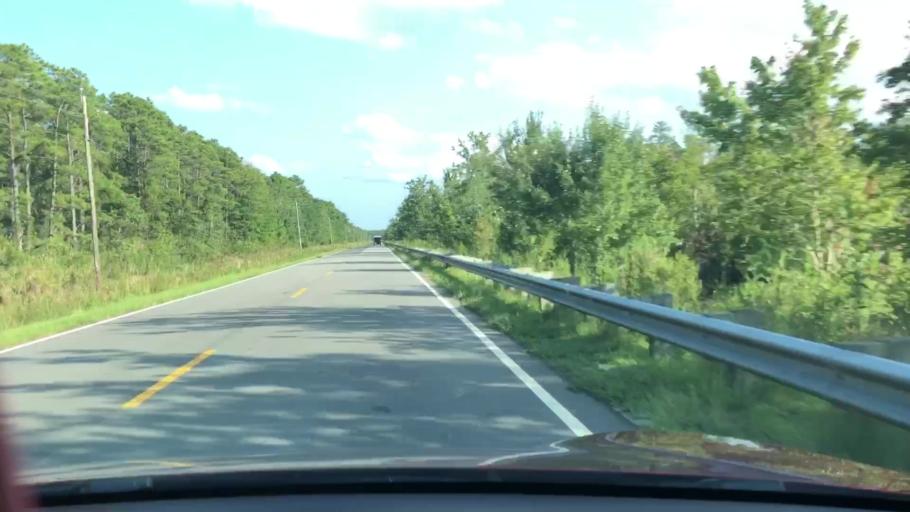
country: US
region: North Carolina
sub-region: Dare County
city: Wanchese
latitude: 35.7976
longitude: -75.7790
